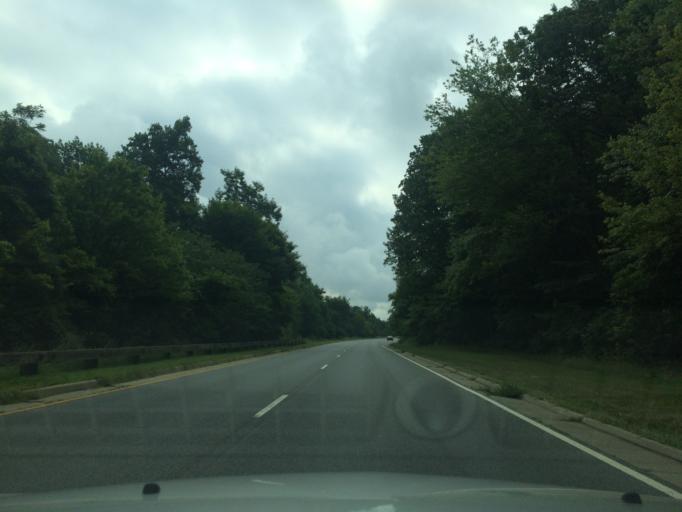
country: US
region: Maryland
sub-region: Prince George's County
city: Silver Hill
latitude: 38.8459
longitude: -76.9378
